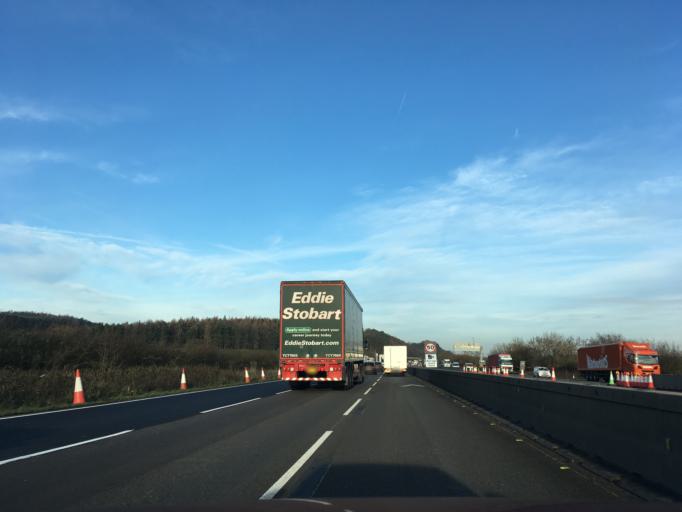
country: GB
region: England
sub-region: Staffordshire
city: Barlaston
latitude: 52.9281
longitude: -2.2101
